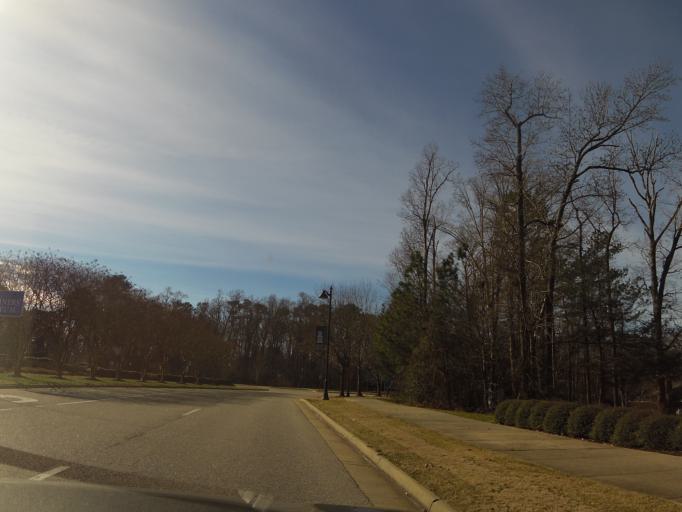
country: US
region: Virginia
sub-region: City of Newport News
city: Newport News
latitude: 37.0608
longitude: -76.4877
